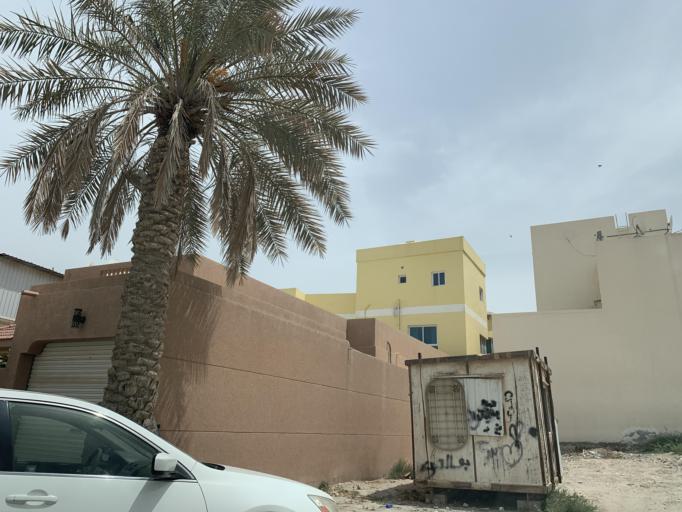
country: BH
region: Northern
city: Ar Rifa'
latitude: 26.1378
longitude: 50.5629
